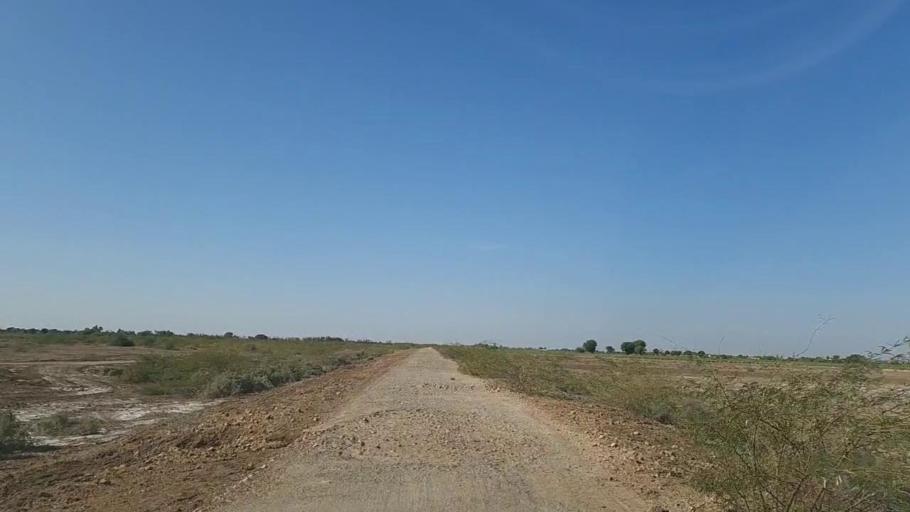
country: PK
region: Sindh
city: Kunri
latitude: 25.2437
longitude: 69.4974
